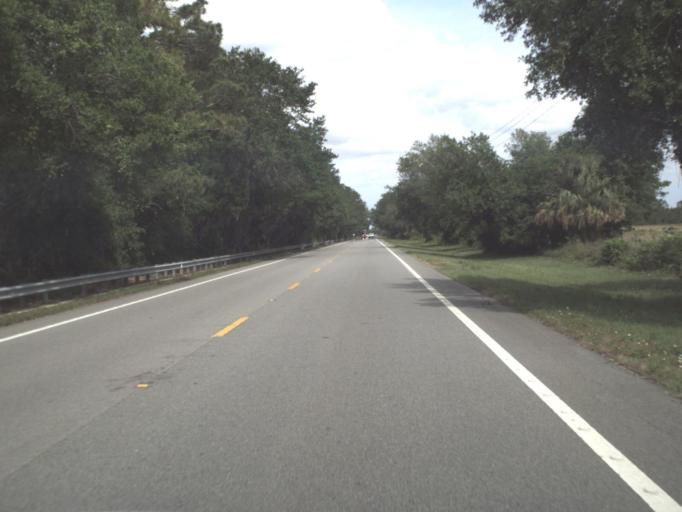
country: US
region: Florida
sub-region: Putnam County
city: Crescent City
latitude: 29.4813
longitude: -81.4036
